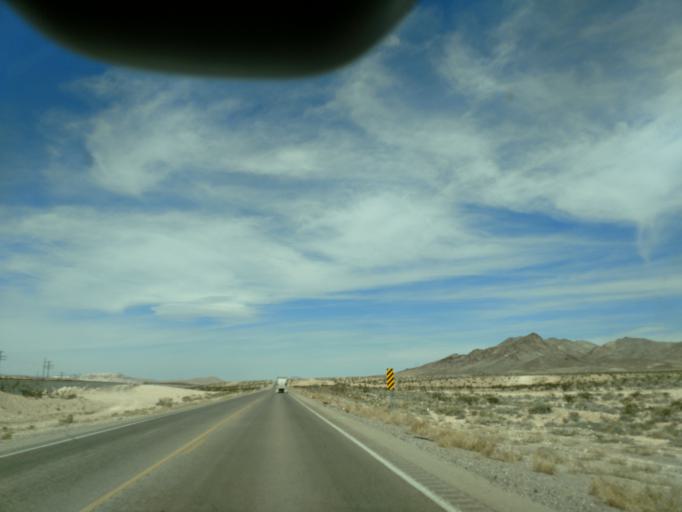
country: US
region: Nevada
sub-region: Clark County
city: Enterprise
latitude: 35.8736
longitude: -115.2327
